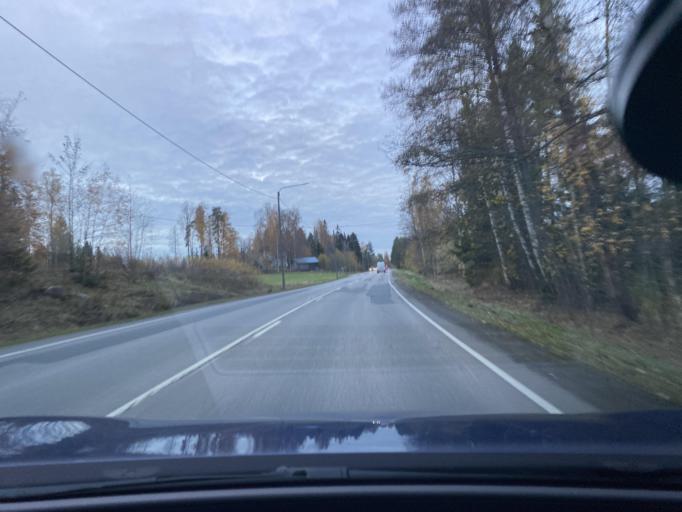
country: FI
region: Uusimaa
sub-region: Helsinki
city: Vihti
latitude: 60.3362
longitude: 24.1993
